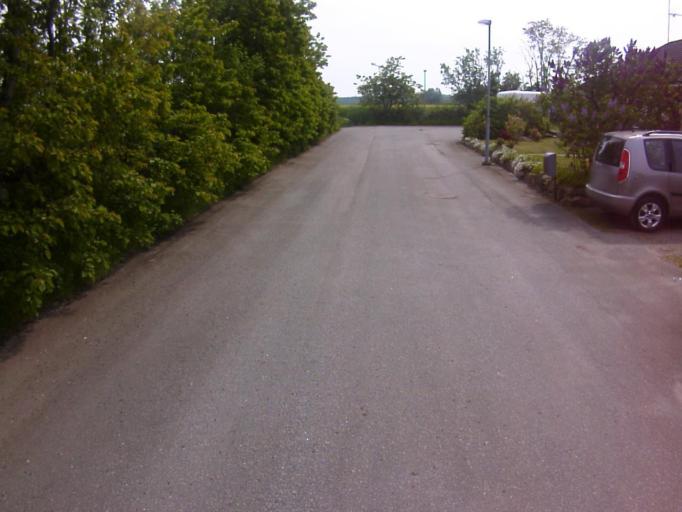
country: SE
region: Blekinge
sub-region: Solvesborgs Kommun
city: Soelvesborg
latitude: 56.0460
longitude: 14.6927
